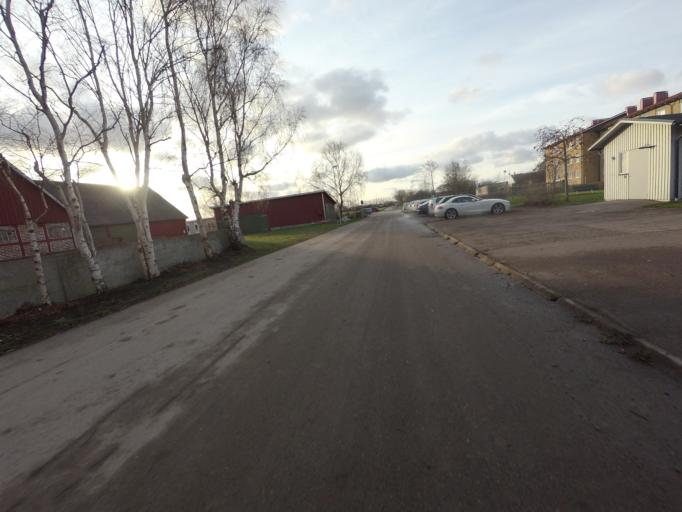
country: SE
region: Skane
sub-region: Hoganas Kommun
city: Hoganas
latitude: 56.1934
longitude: 12.5709
